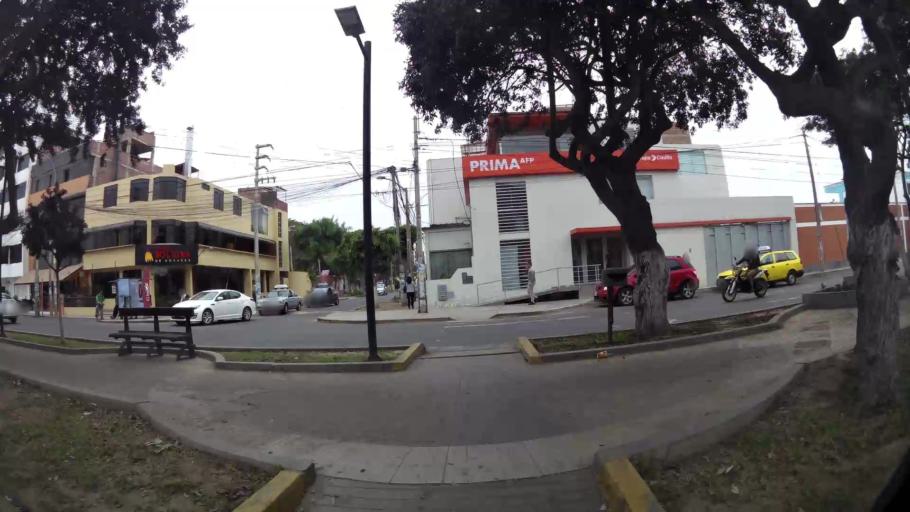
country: PE
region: La Libertad
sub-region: Provincia de Trujillo
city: Buenos Aires
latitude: -8.1278
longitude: -79.0365
